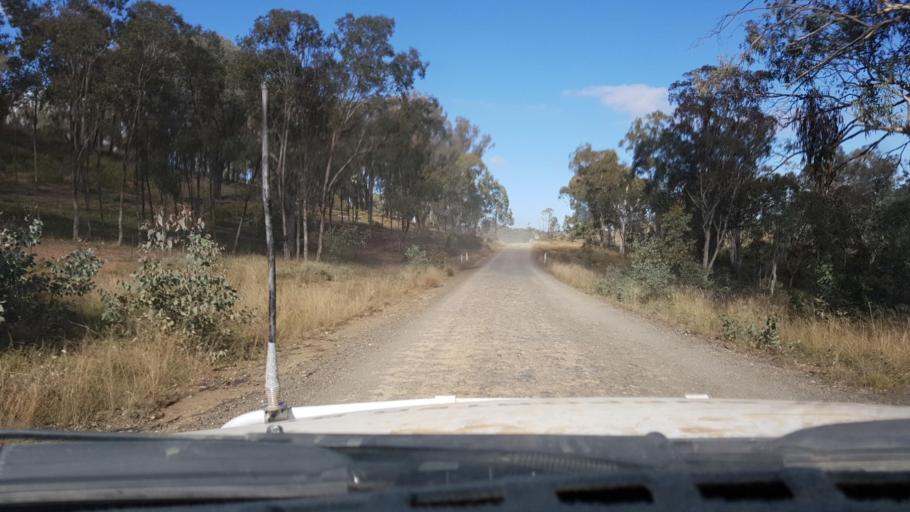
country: AU
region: New South Wales
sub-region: Tamworth Municipality
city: Manilla
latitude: -30.4646
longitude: 150.7435
